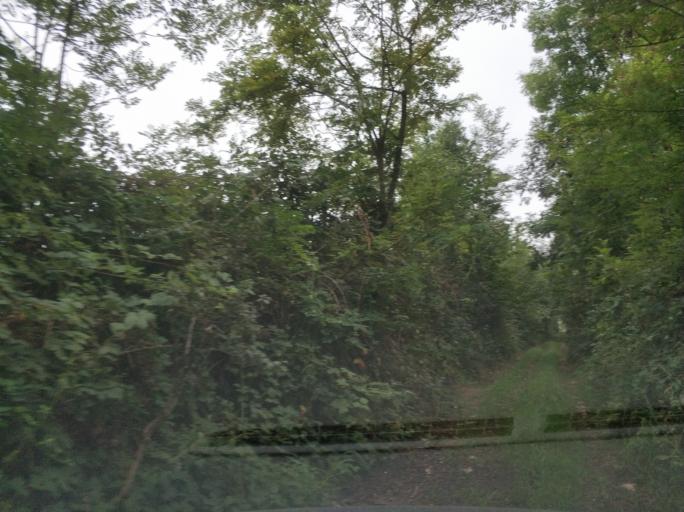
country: IT
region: Piedmont
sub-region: Provincia di Torino
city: San Francesco al Campo
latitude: 45.2313
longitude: 7.6851
